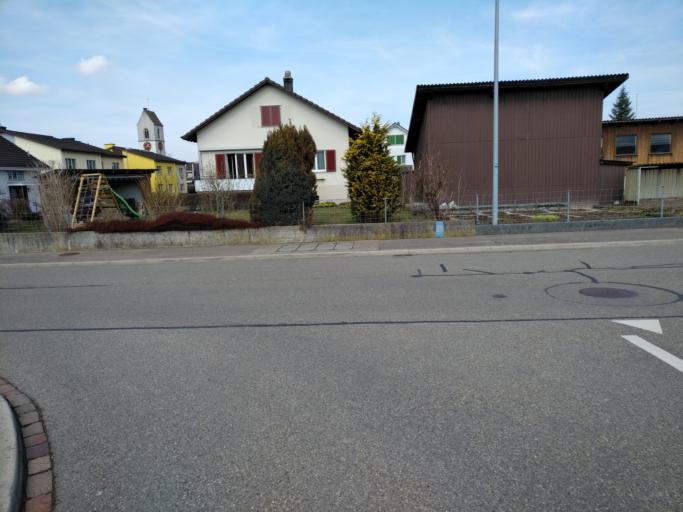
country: CH
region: Zurich
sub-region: Bezirk Winterthur
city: Wiesendangen / Wiesendangen (Dorf)
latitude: 47.5198
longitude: 8.7912
